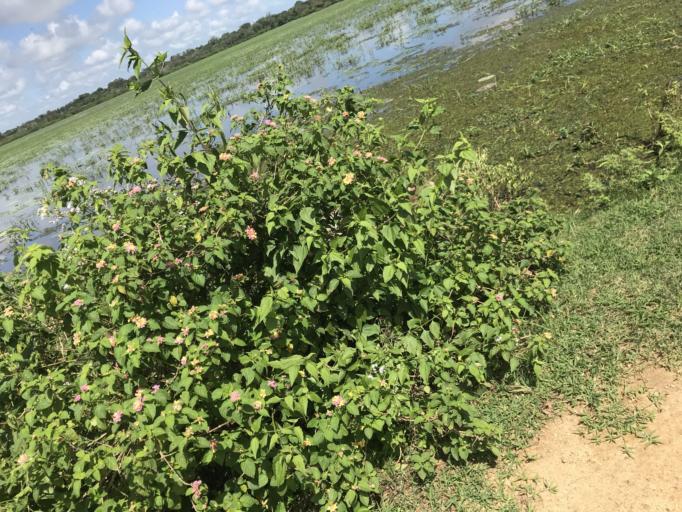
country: LK
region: Uva
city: Wattegama
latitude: 6.8527
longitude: 81.7745
